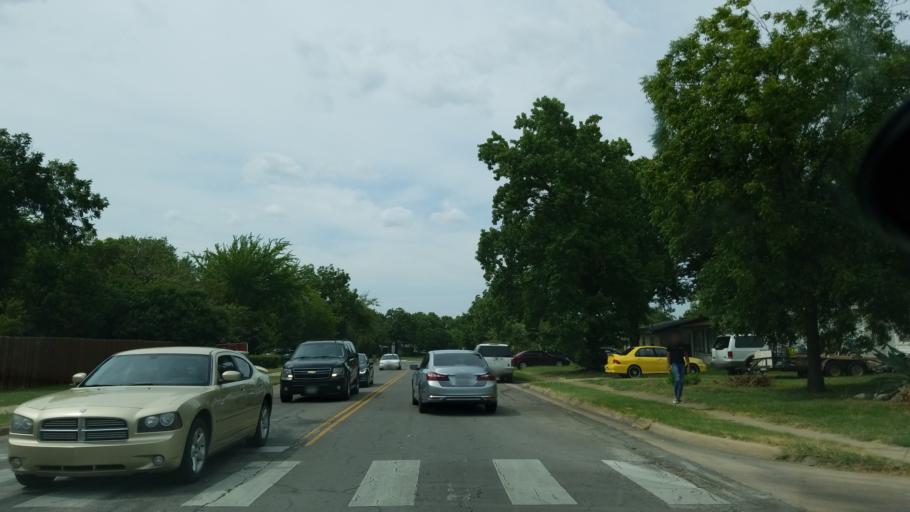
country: US
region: Texas
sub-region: Tarrant County
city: Arlington
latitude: 32.7315
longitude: -97.0836
